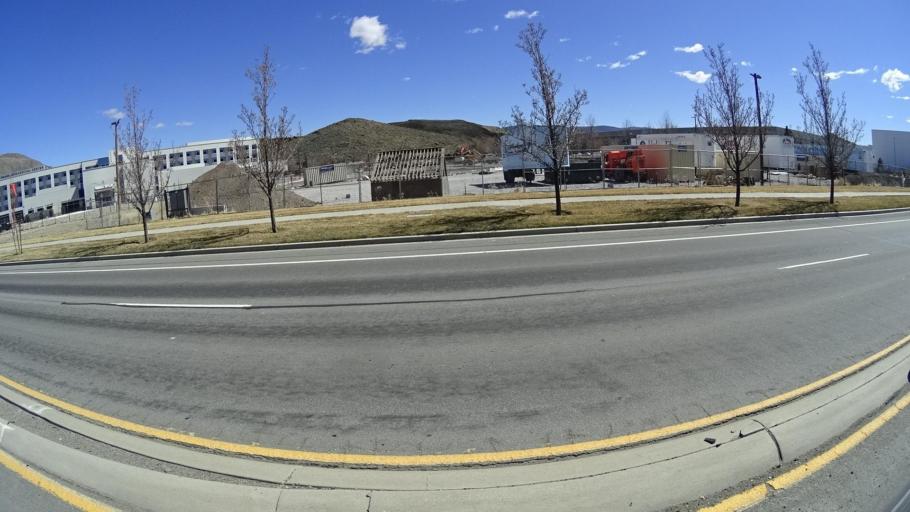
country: US
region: Nevada
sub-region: Washoe County
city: Sparks
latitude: 39.4655
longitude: -119.7705
